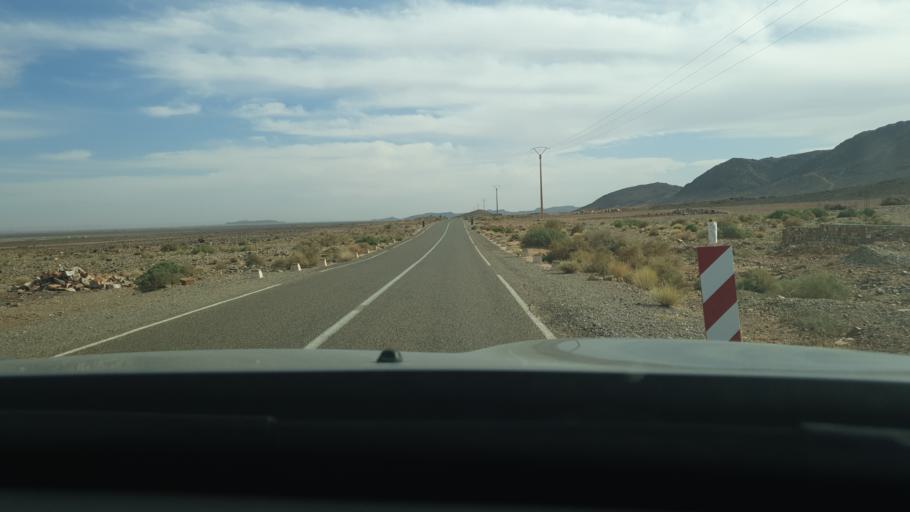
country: MA
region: Meknes-Tafilalet
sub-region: Errachidia
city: Fezna
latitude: 31.5277
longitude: -4.6336
